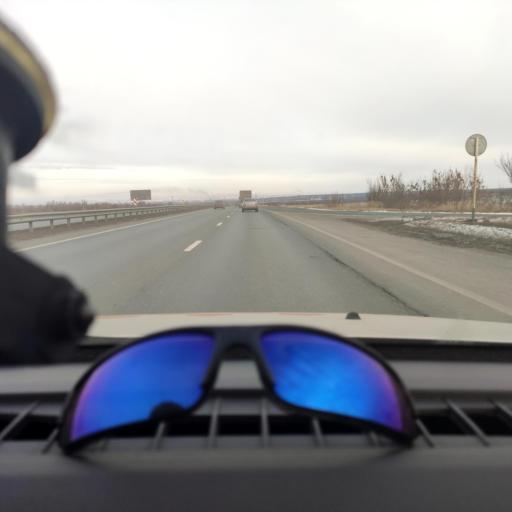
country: RU
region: Samara
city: Novokuybyshevsk
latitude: 53.0109
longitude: 49.9772
